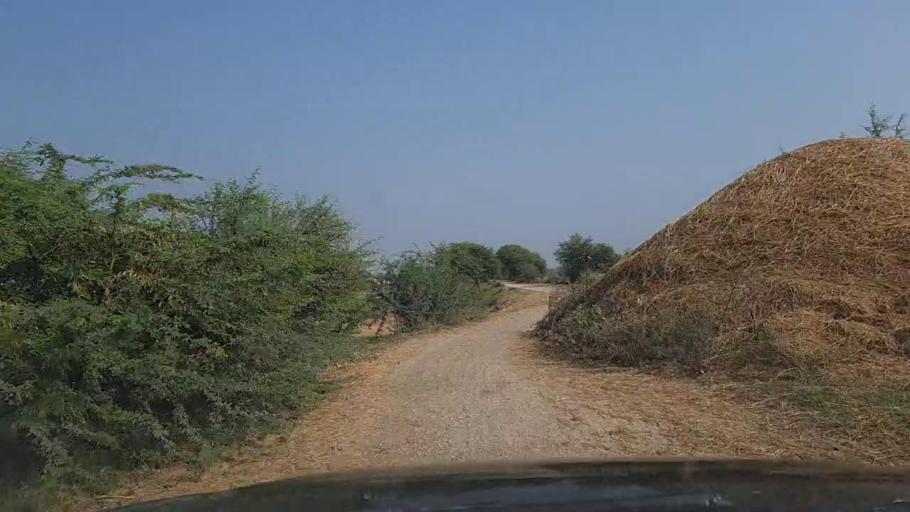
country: PK
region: Sindh
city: Mirpur Batoro
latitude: 24.6964
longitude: 68.2441
